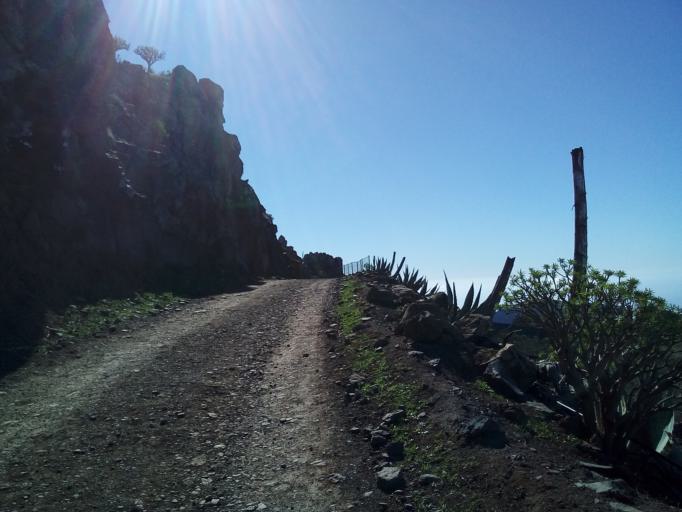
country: ES
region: Canary Islands
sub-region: Provincia de Santa Cruz de Tenerife
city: Vallehermosa
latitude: 28.1273
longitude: -17.3276
